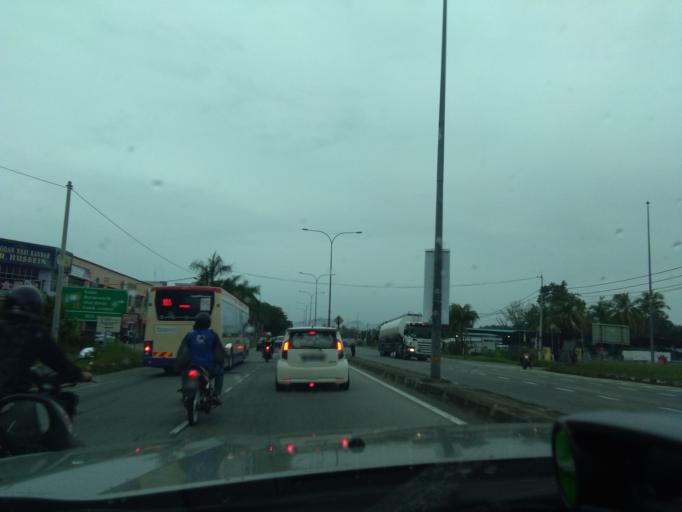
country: MY
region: Penang
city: Nibong Tebal
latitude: 5.1814
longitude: 100.4844
